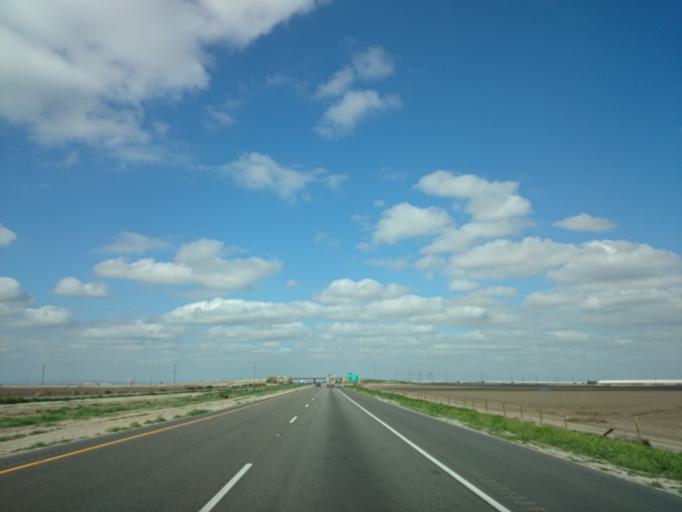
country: US
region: California
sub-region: Kern County
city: Greenfield
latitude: 35.1570
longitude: -119.1054
